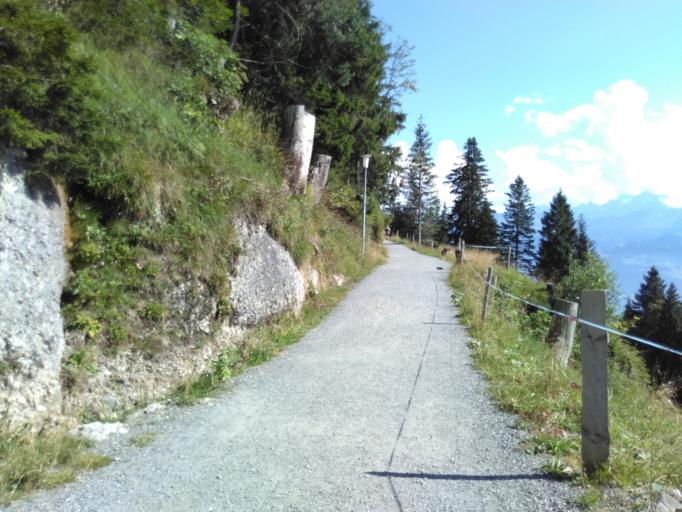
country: CH
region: Lucerne
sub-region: Lucerne-Land District
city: Weggis
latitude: 47.0451
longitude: 8.4579
